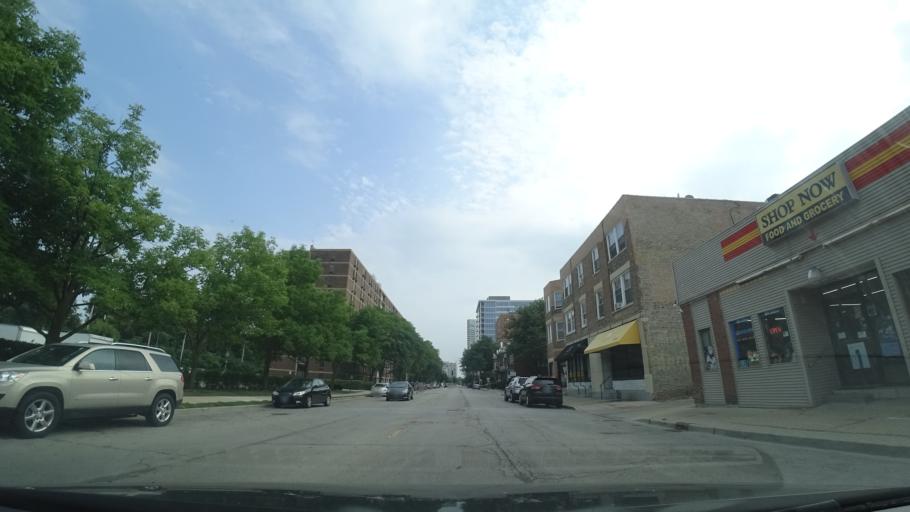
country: US
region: Illinois
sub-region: Cook County
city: Evanston
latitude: 42.0537
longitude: -87.6847
